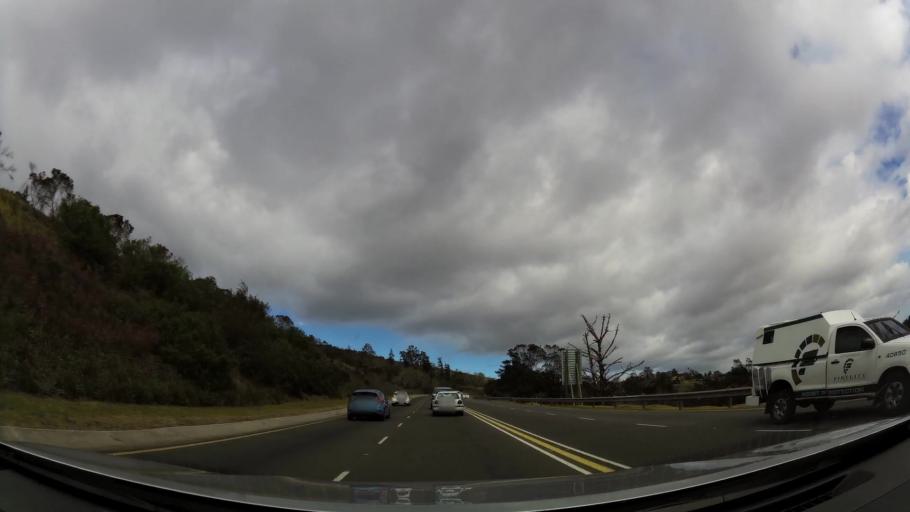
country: ZA
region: Western Cape
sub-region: Eden District Municipality
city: George
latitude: -33.9884
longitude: 22.5400
